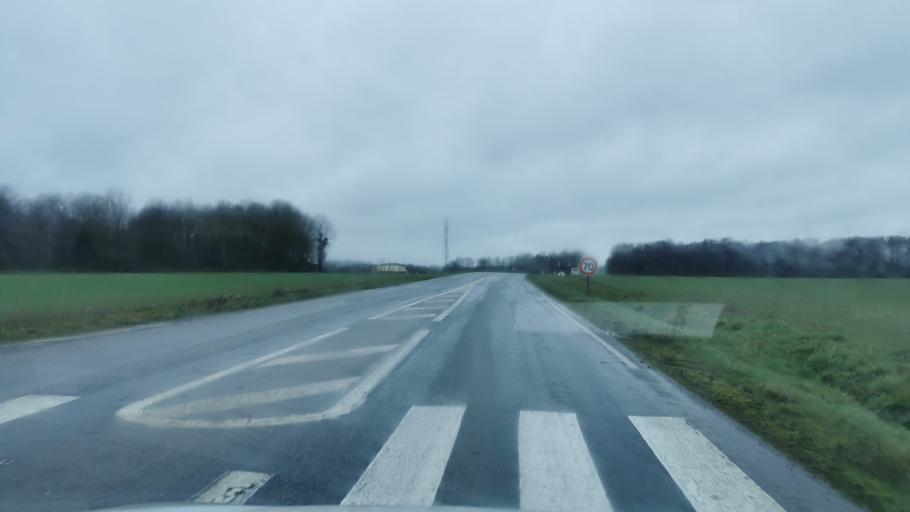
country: FR
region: Haute-Normandie
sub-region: Departement de l'Eure
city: Normanville
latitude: 49.0875
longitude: 1.1786
